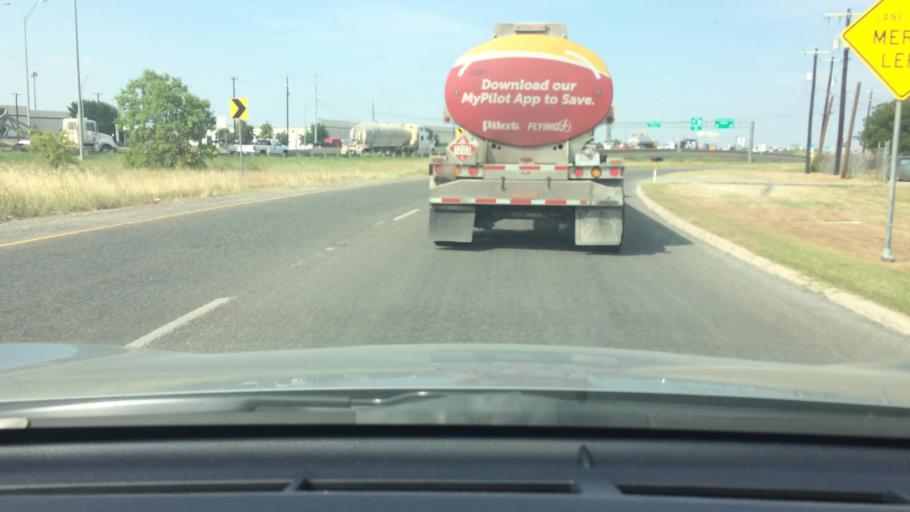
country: US
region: Texas
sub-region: Bexar County
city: Kirby
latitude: 29.4362
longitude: -98.3867
